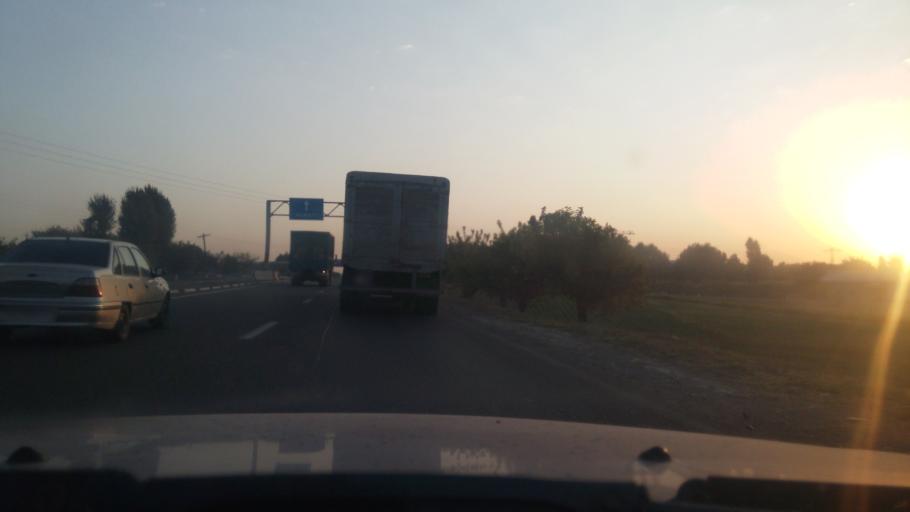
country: UZ
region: Toshkent
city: Yangiyul
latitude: 41.1040
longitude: 68.9718
